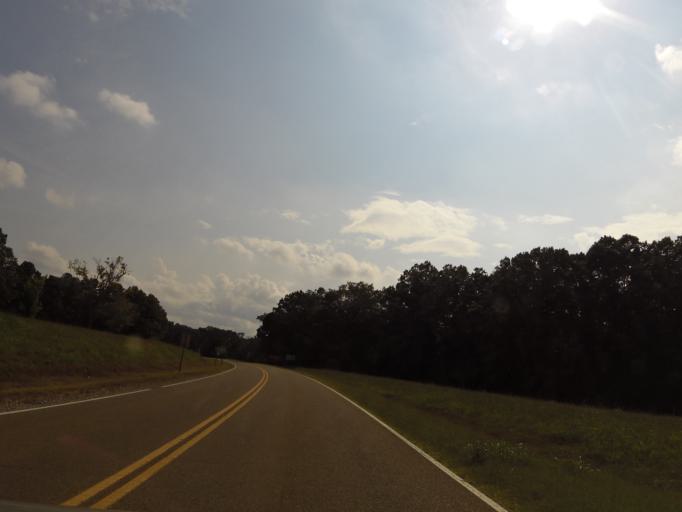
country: US
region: Tennessee
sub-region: Hardin County
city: Crump
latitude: 35.1396
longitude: -88.3596
